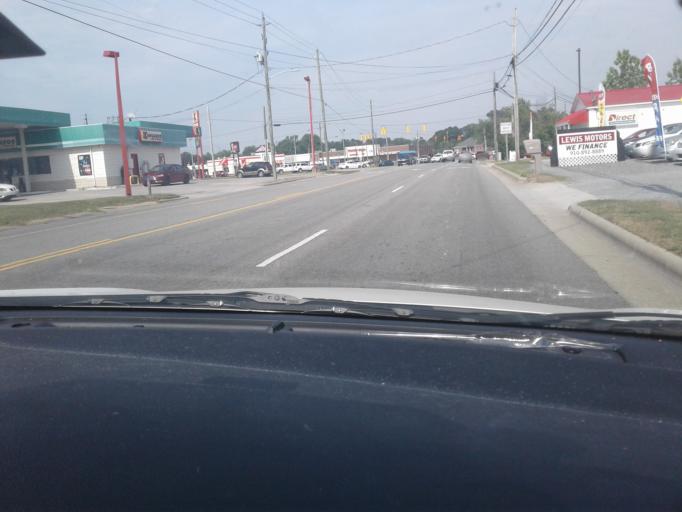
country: US
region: North Carolina
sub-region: Harnett County
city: Dunn
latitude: 35.3153
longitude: -78.6265
